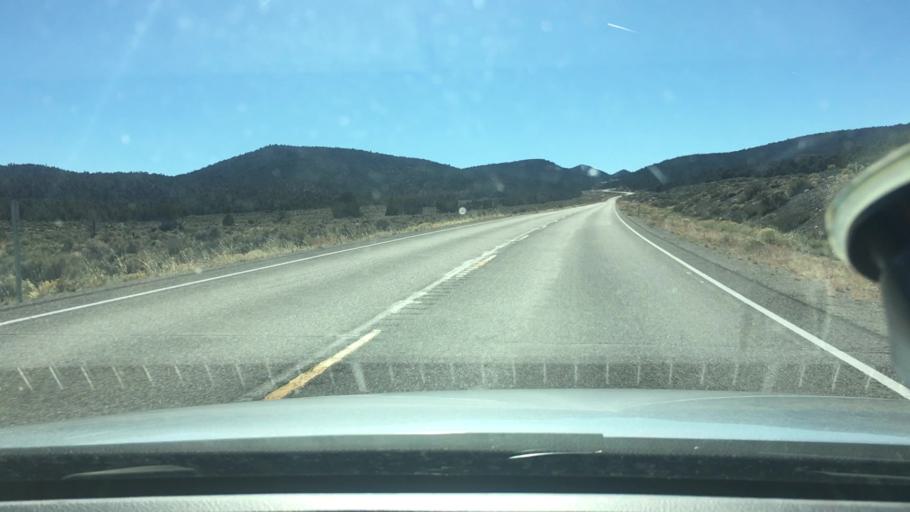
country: US
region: Nevada
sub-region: White Pine County
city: Ely
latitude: 38.8350
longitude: -115.2586
